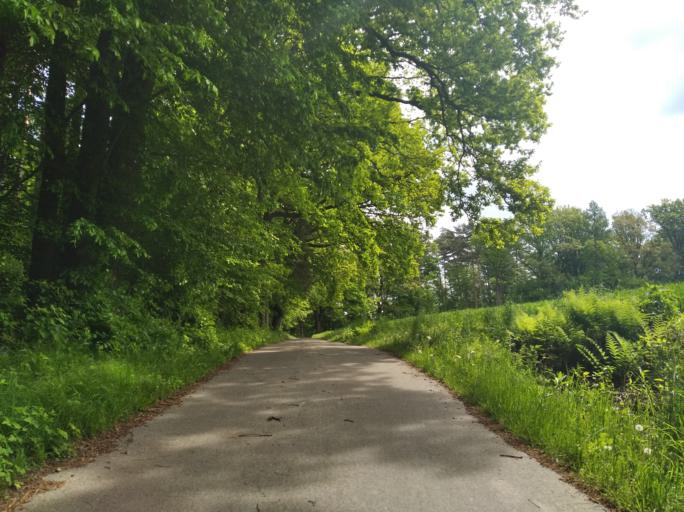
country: PL
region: Subcarpathian Voivodeship
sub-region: Powiat strzyzowski
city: Czudec
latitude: 49.9291
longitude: 21.8270
